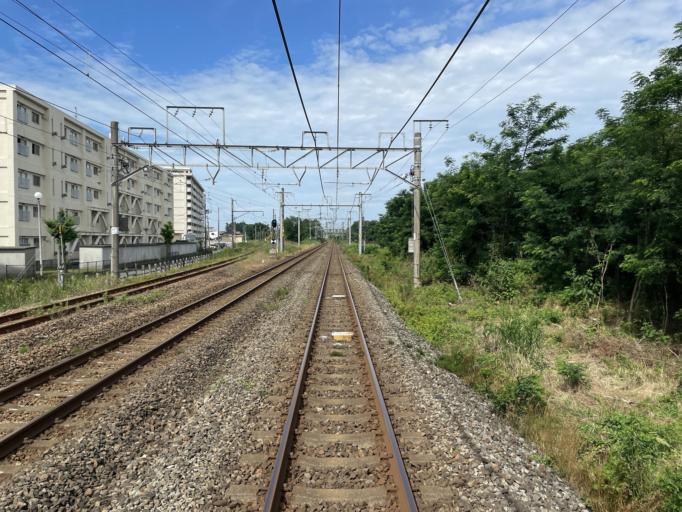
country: JP
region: Niigata
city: Kameda-honcho
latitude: 37.9048
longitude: 139.0976
